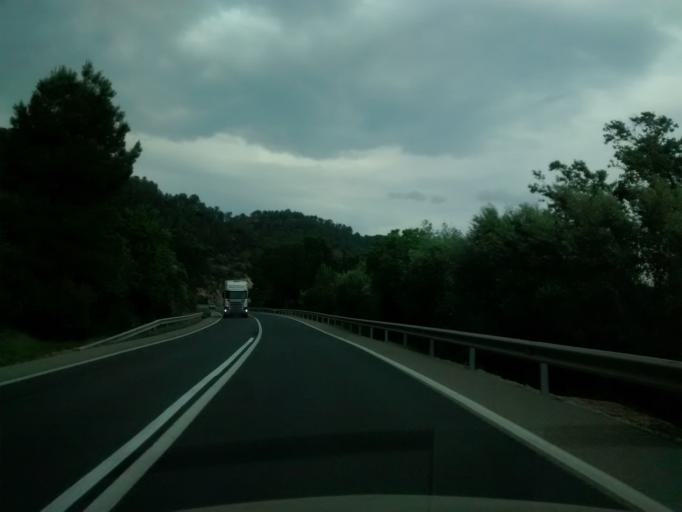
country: ES
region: Catalonia
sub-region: Provincia de Tarragona
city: Benifallet
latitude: 40.9692
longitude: 0.5101
